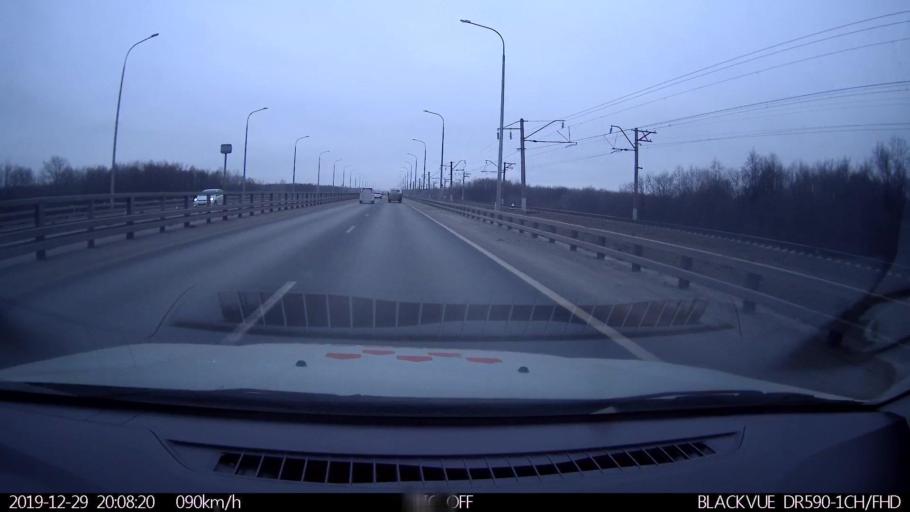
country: RU
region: Nizjnij Novgorod
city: Neklyudovo
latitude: 56.3877
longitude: 43.9701
